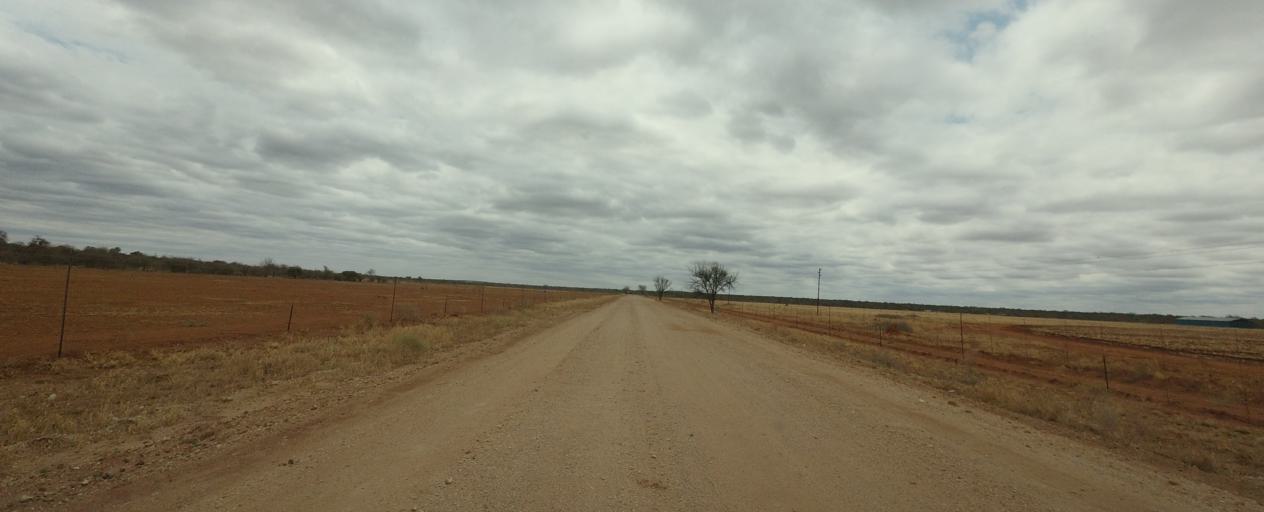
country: BW
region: Central
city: Mathathane
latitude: -22.7101
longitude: 28.5731
